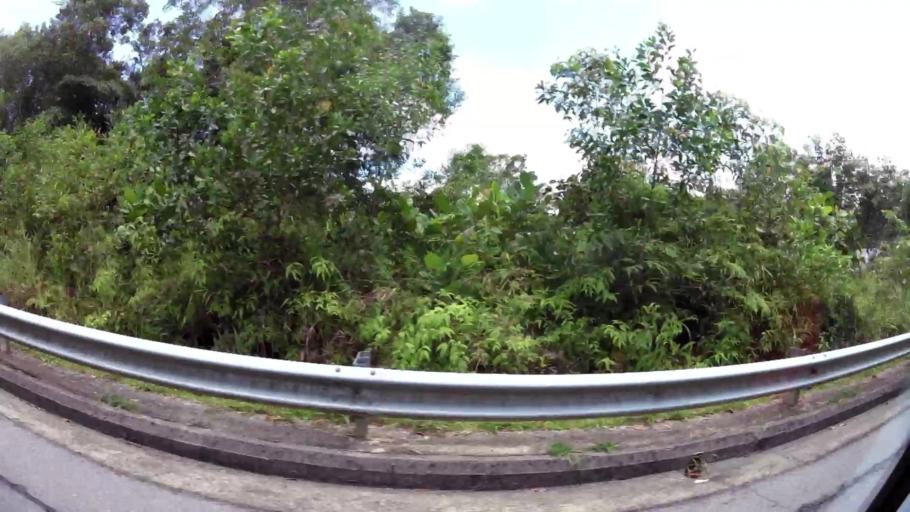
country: BN
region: Brunei and Muara
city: Bandar Seri Begawan
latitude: 4.9291
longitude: 114.9626
